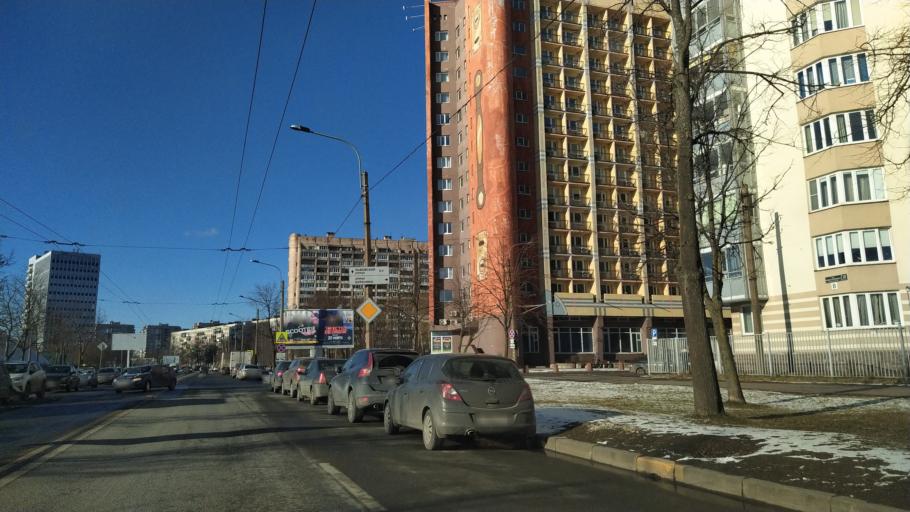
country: RU
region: Leningrad
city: Kalininskiy
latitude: 59.9692
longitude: 30.4261
